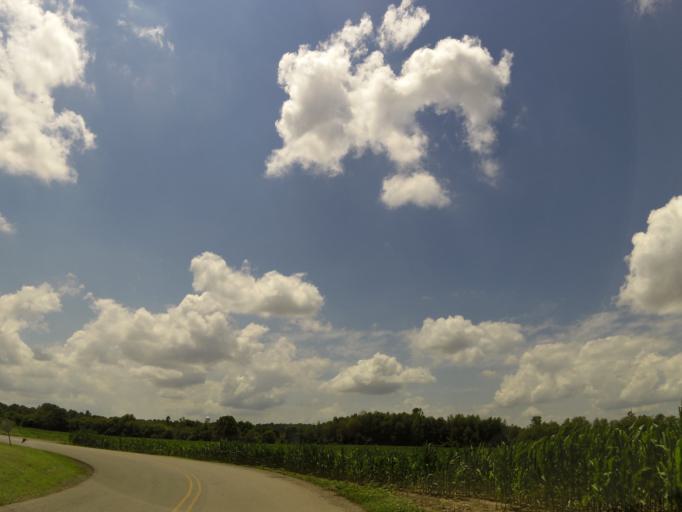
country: US
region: Kentucky
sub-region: Fulton County
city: Hickman
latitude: 36.5664
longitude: -89.2120
